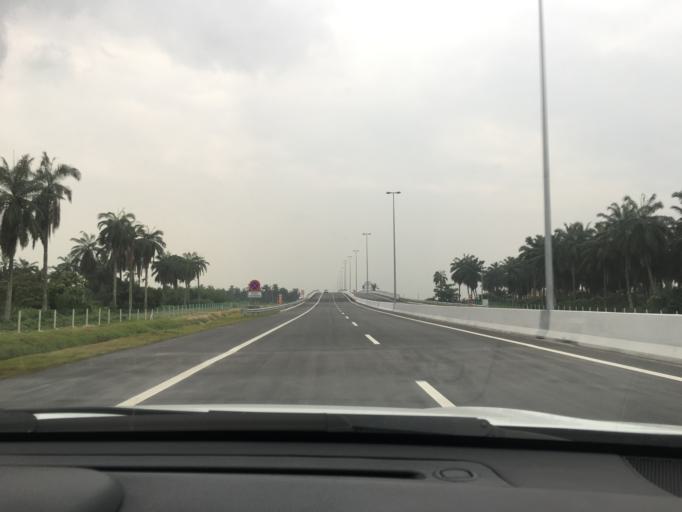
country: MY
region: Selangor
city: Klang
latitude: 3.1154
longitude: 101.4112
